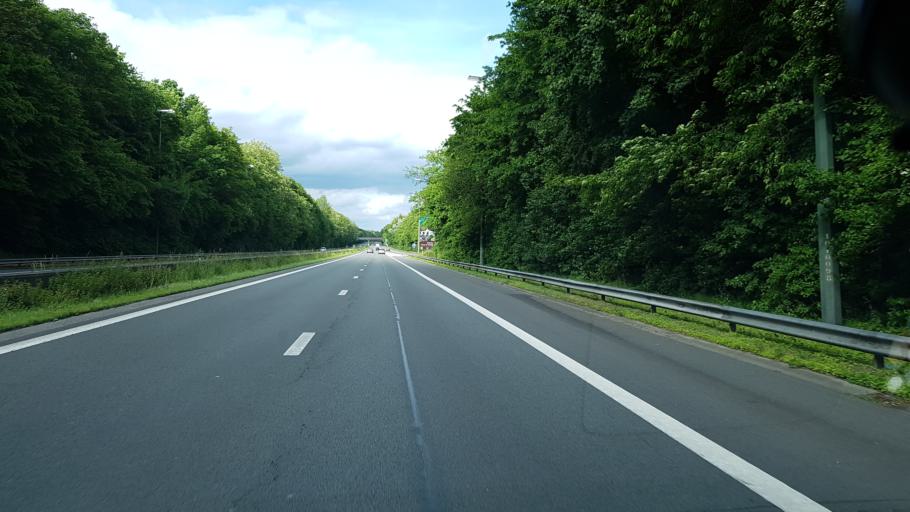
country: BE
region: Wallonia
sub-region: Province du Brabant Wallon
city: Braine-l'Alleud
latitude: 50.6692
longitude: 4.3891
